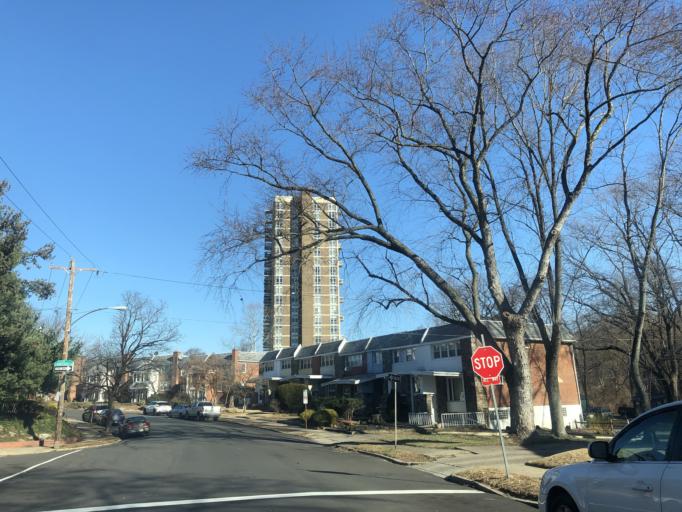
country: US
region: Pennsylvania
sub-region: Montgomery County
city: Bala-Cynwyd
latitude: 40.0022
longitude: -75.2032
